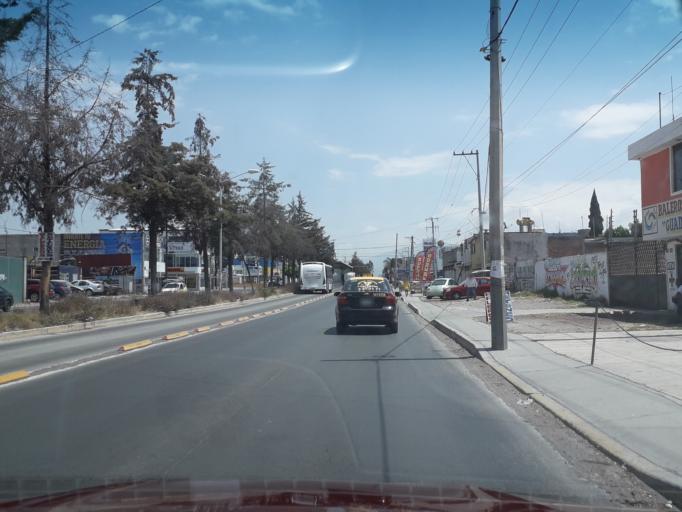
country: MX
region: Puebla
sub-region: Puebla
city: El Capulo (La Quebradora)
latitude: 18.9795
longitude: -98.2545
